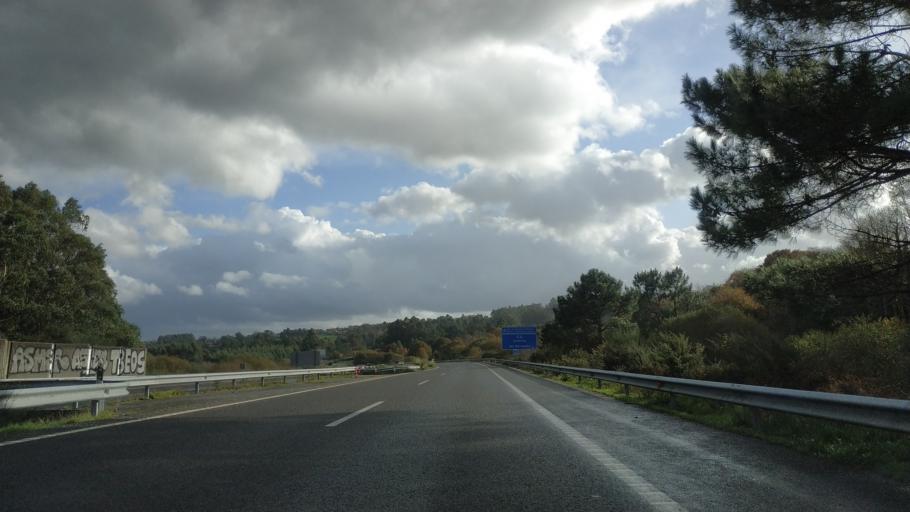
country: ES
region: Galicia
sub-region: Provincia da Coruna
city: Cambre
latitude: 43.2718
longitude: -8.3606
